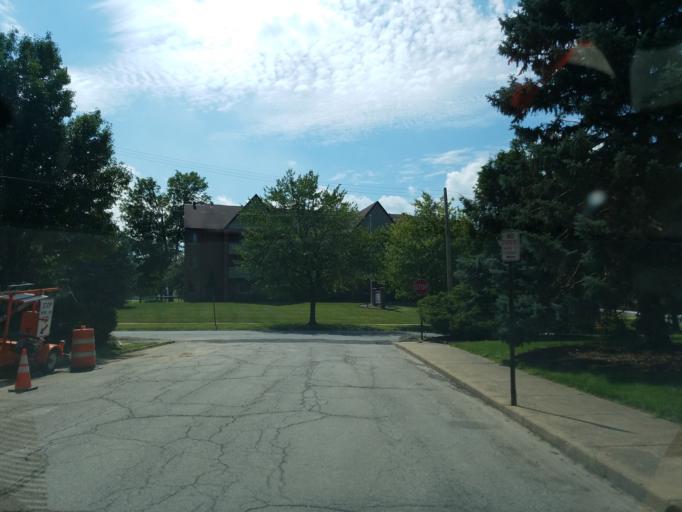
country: US
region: Ohio
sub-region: Ashland County
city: Ashland
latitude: 40.8628
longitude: -82.3120
